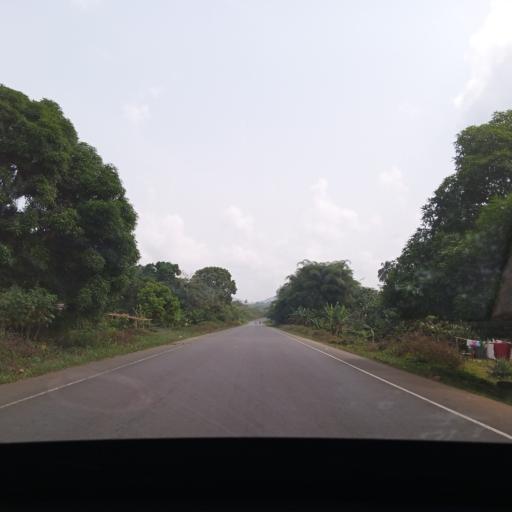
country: LR
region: Margibi
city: Kakata
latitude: 6.2539
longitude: -10.3105
